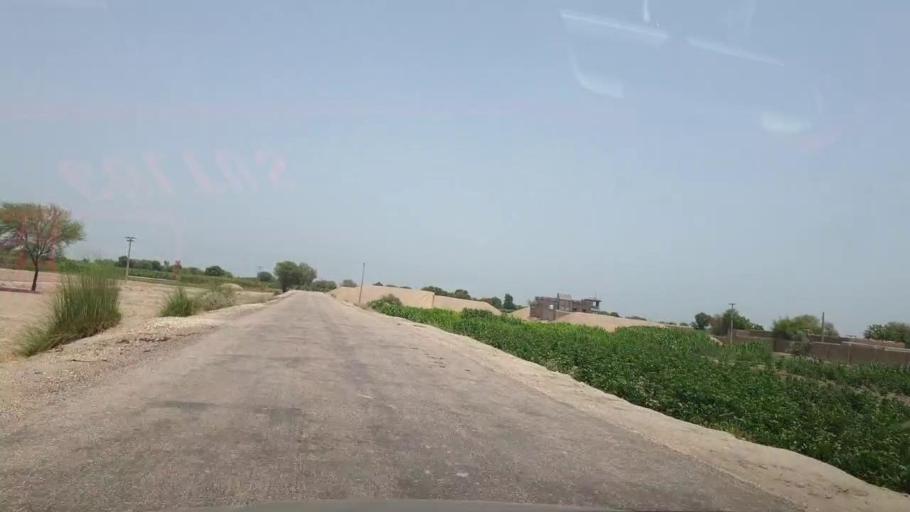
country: PK
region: Sindh
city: Daulatpur
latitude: 26.3889
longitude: 68.0577
